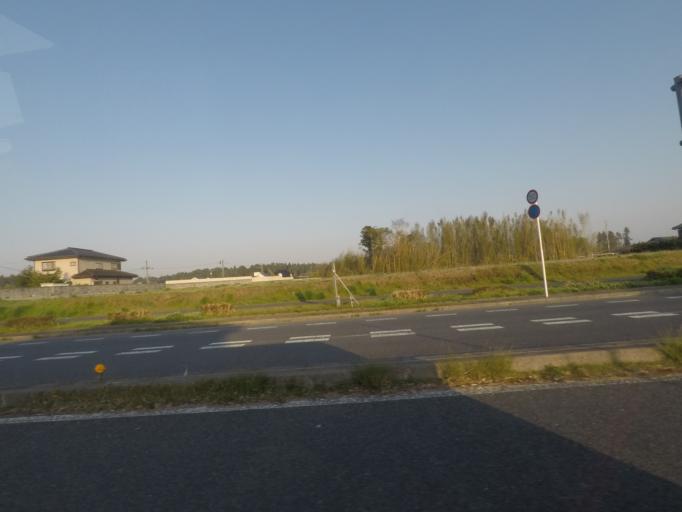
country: JP
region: Chiba
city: Shisui
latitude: 35.7170
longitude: 140.2618
